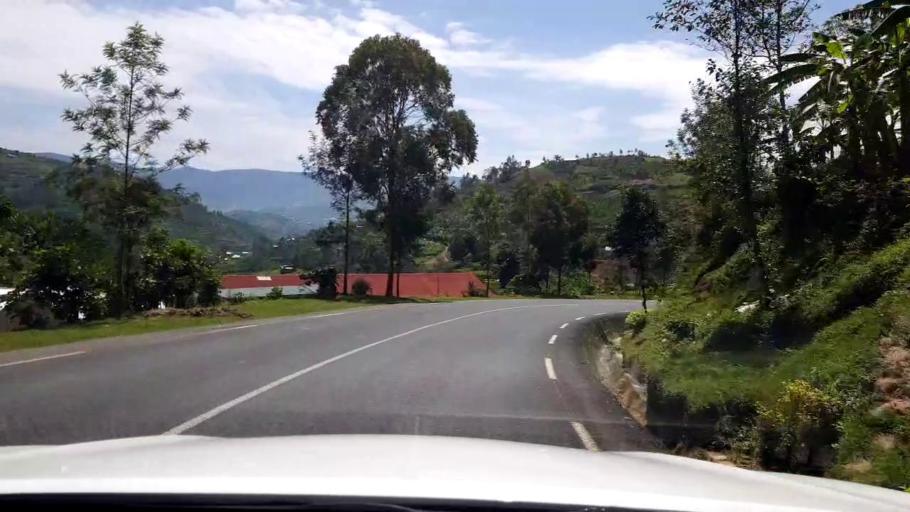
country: RW
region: Southern Province
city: Gitarama
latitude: -1.9188
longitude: 29.6380
